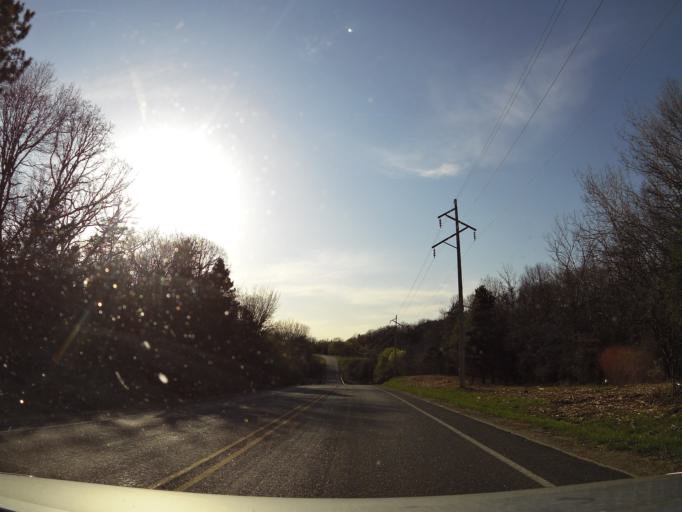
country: US
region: Wisconsin
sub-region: Pierce County
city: River Falls
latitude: 44.8322
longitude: -92.6371
